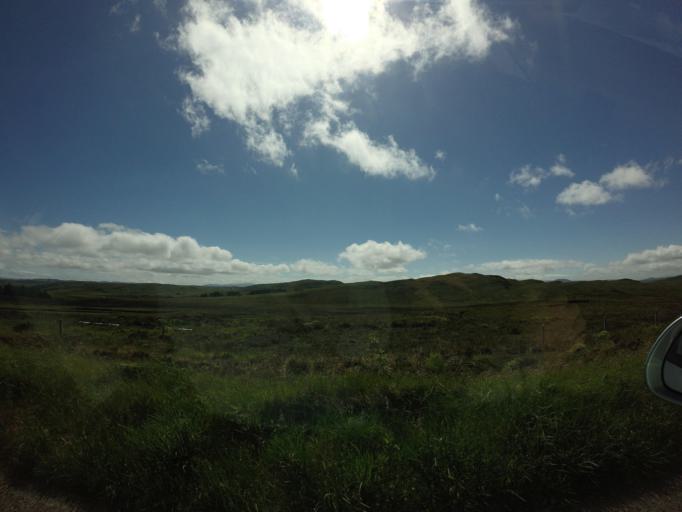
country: GB
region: Scotland
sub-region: Eilean Siar
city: Stornoway
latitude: 58.1551
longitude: -6.5091
